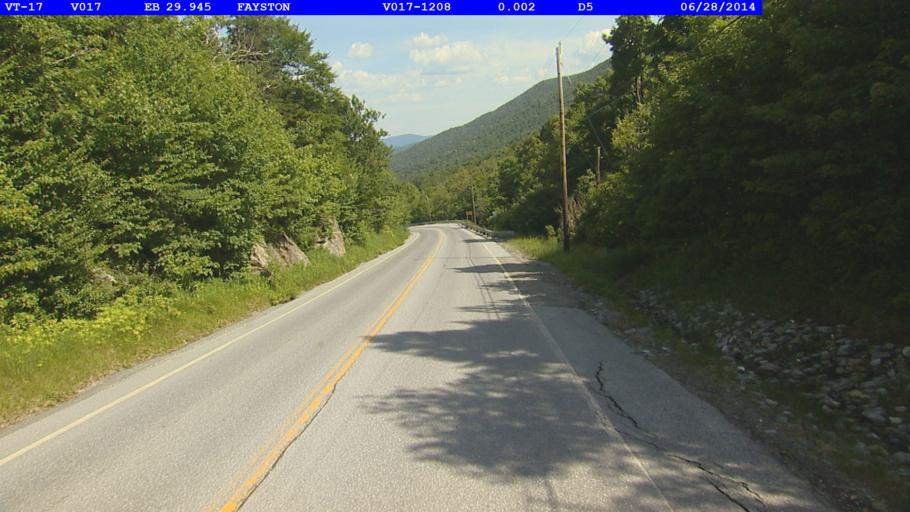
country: US
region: Vermont
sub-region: Addison County
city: Bristol
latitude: 44.2087
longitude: -72.9291
